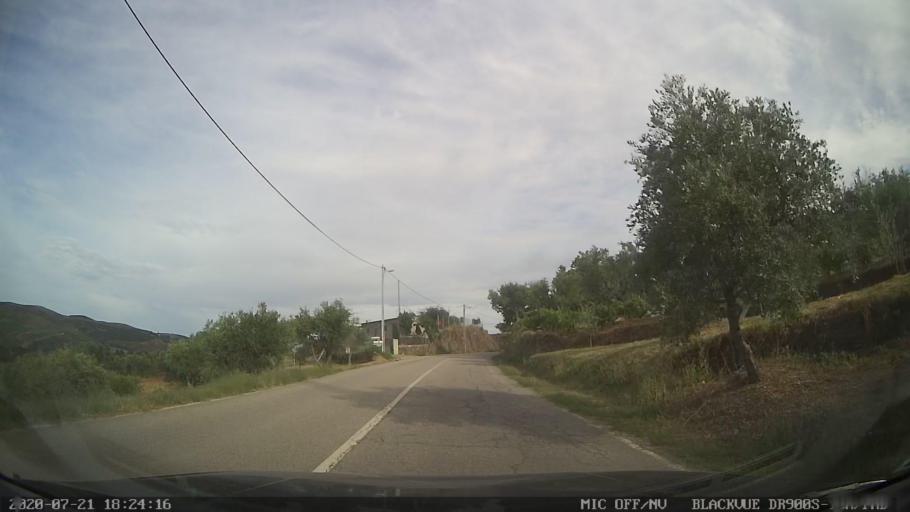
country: PT
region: Guarda
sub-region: Vila Nova de Foz Coa
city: Custoias
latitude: 41.0707
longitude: -7.3897
